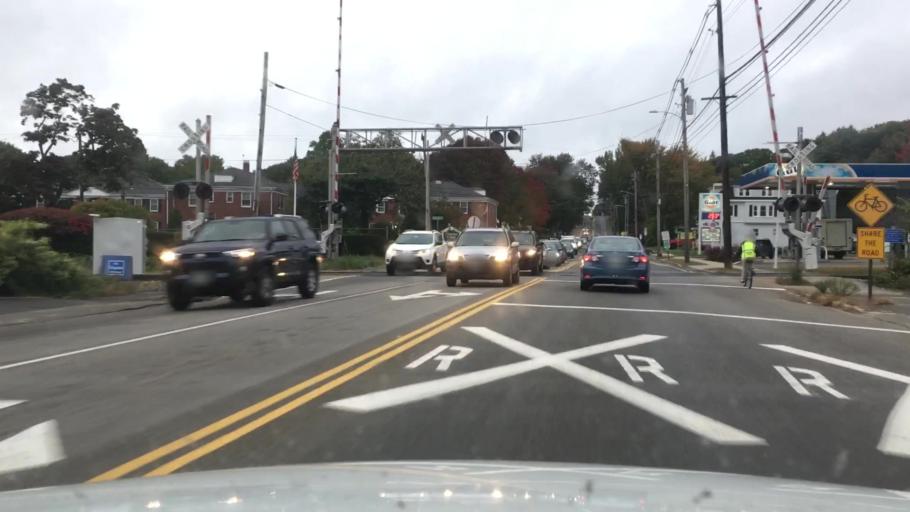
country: US
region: Maine
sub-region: Cumberland County
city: Portland
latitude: 43.6636
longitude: -70.2850
